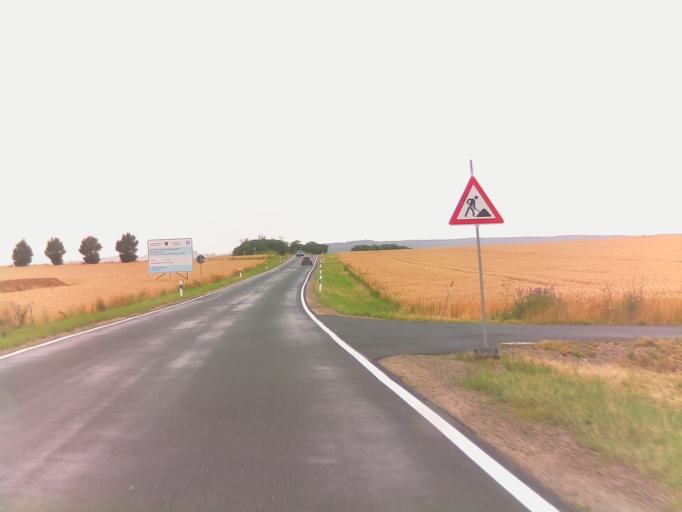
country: DE
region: Thuringia
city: Rottenbach
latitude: 50.7390
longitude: 11.1607
